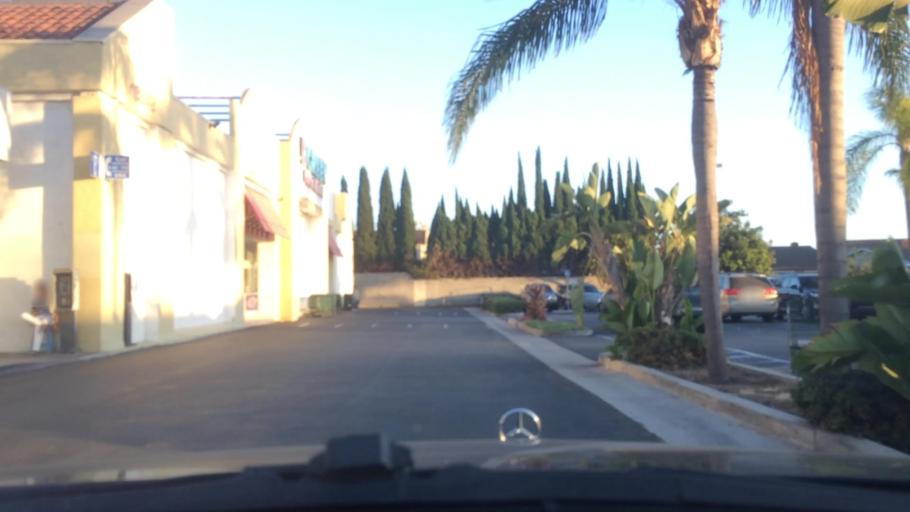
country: US
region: California
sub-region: Orange County
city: Midway City
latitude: 33.7301
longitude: -117.9711
